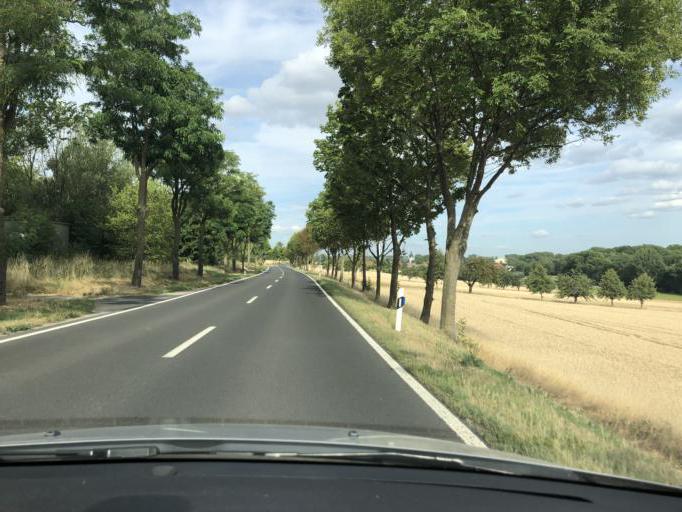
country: DE
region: Thuringia
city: Eberstedt
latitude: 51.0318
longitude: 11.5846
